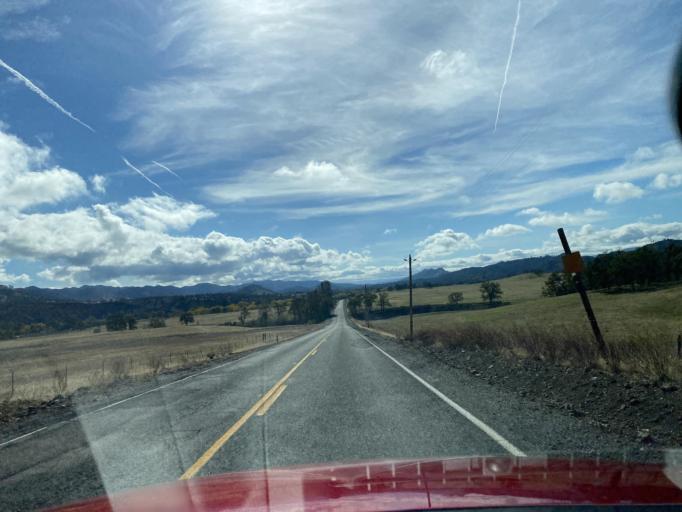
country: US
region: California
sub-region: Glenn County
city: Willows
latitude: 39.4731
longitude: -122.5133
